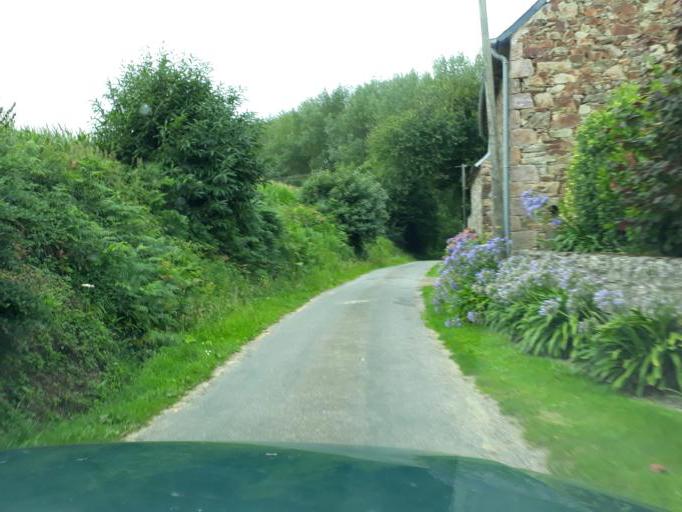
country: FR
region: Brittany
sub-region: Departement des Cotes-d'Armor
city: Paimpol
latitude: 48.7741
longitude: -3.0718
